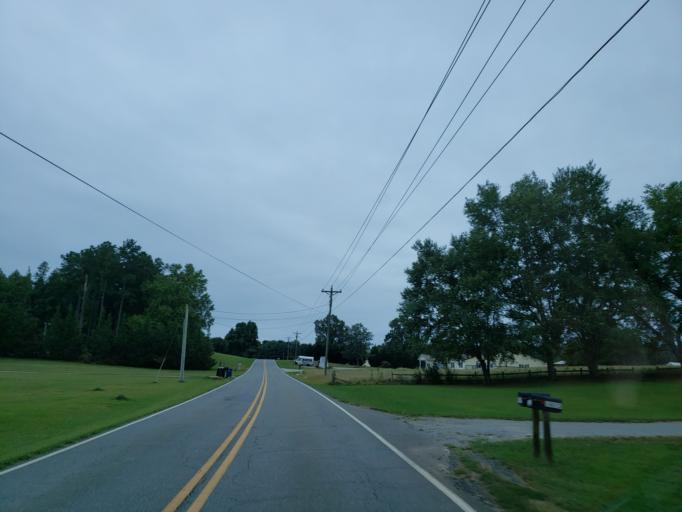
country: US
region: Georgia
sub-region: Cherokee County
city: Canton
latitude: 34.3480
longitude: -84.4910
